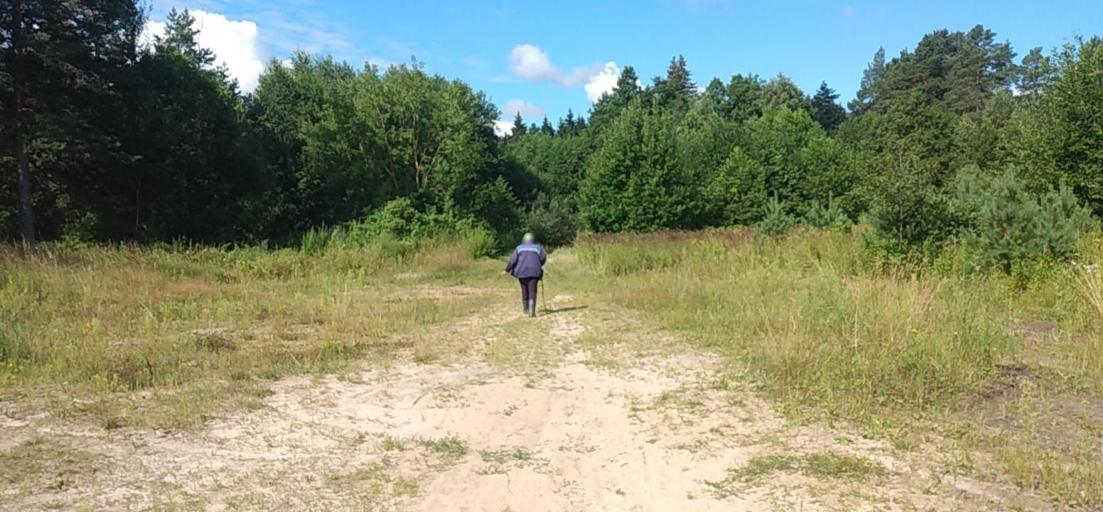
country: RU
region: Moskovskaya
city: Reshetnikovo
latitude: 56.4441
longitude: 36.5520
